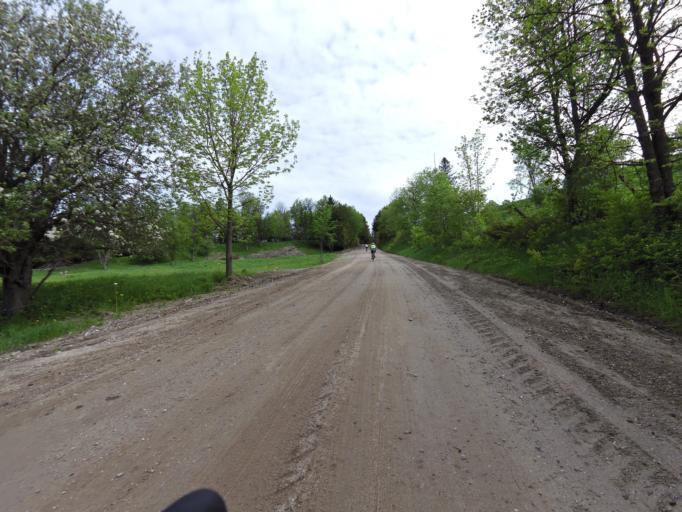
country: CA
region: Quebec
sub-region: Outaouais
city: Wakefield
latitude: 45.7314
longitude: -75.8903
